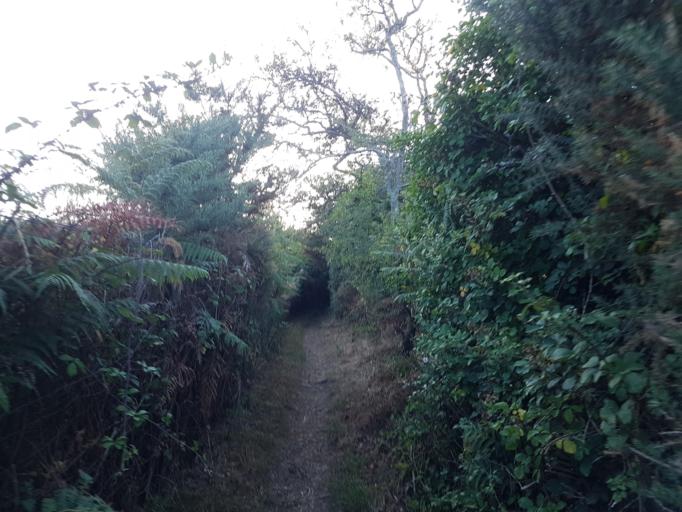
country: FR
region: Brittany
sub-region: Departement du Morbihan
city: Etel
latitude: 47.6839
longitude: -3.2073
